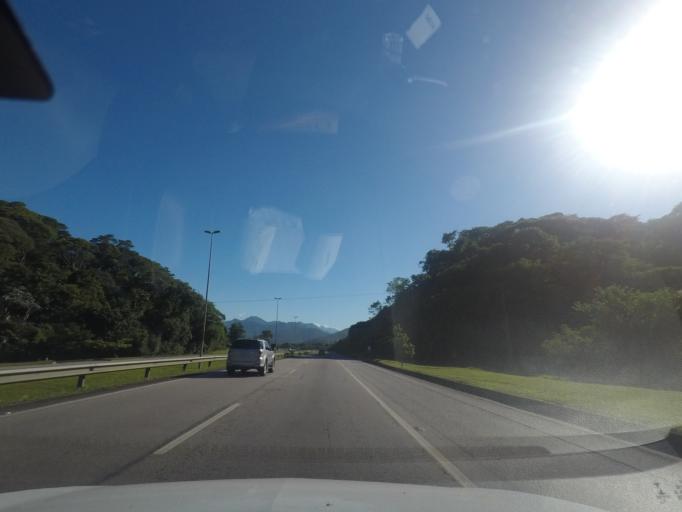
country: BR
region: Rio de Janeiro
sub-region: Guapimirim
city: Guapimirim
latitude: -22.5697
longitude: -43.0046
